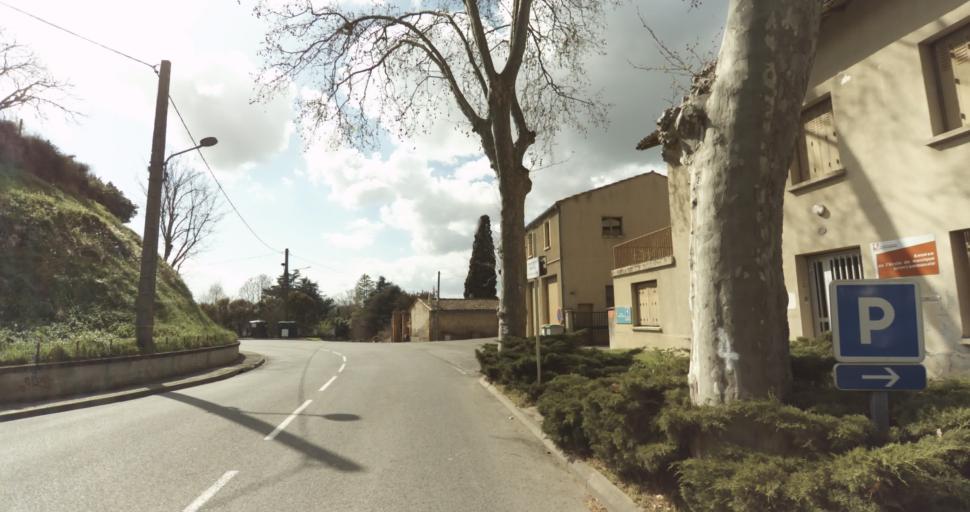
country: FR
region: Midi-Pyrenees
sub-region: Departement de la Haute-Garonne
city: Auterive
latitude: 43.3540
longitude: 1.4774
